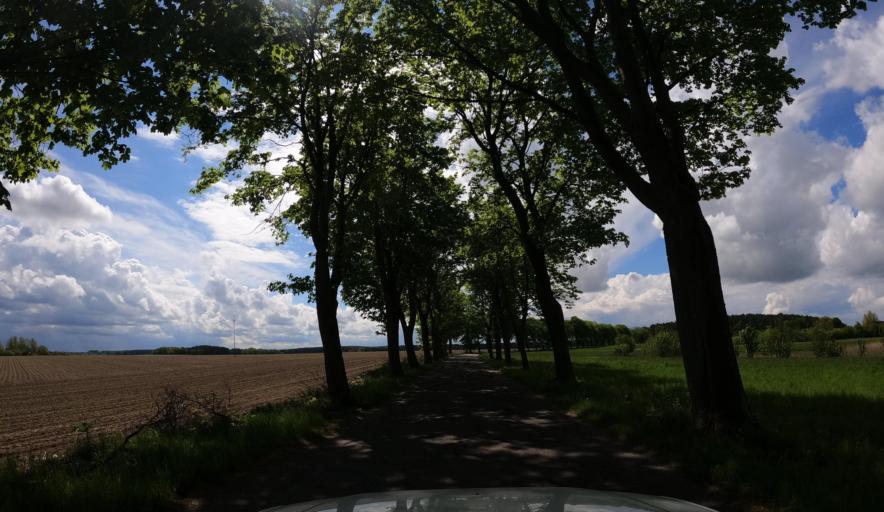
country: PL
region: West Pomeranian Voivodeship
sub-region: Powiat kamienski
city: Wolin
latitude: 53.8937
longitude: 14.6645
